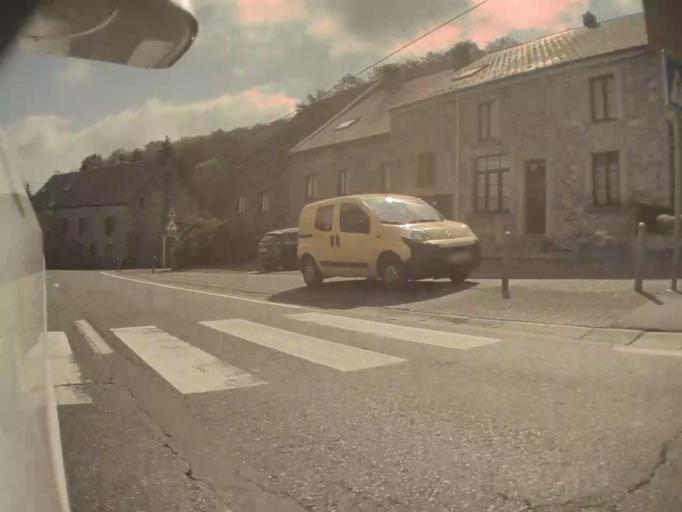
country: BE
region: Wallonia
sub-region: Province du Luxembourg
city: Tellin
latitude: 50.0817
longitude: 5.2202
